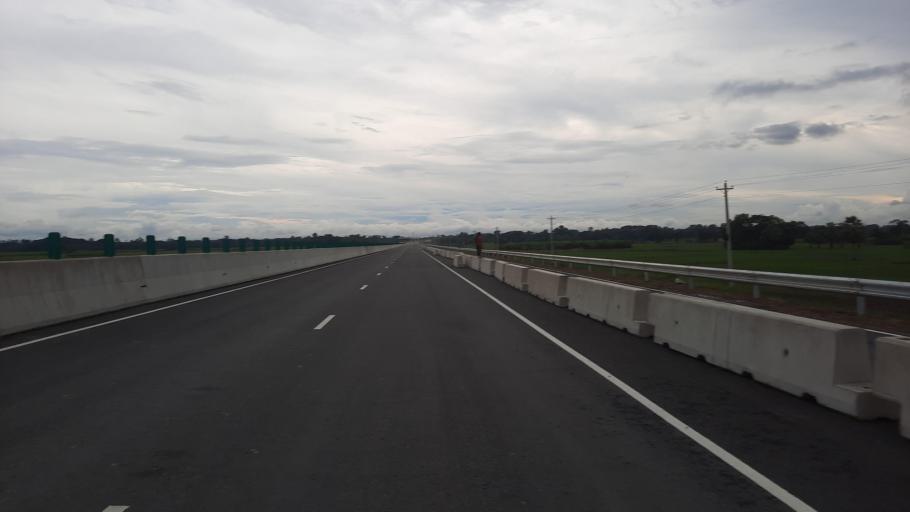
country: BD
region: Khulna
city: Kalia
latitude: 23.2034
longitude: 89.7087
